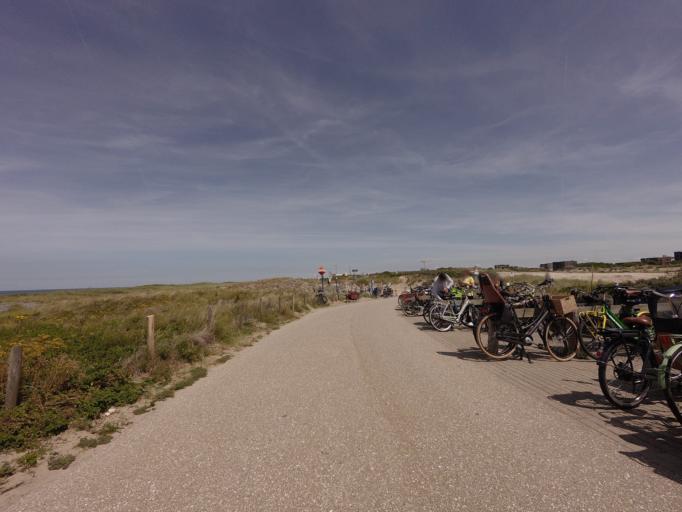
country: NL
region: South Holland
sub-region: Gemeente Den Haag
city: Scheveningen
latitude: 52.0917
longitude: 4.2515
